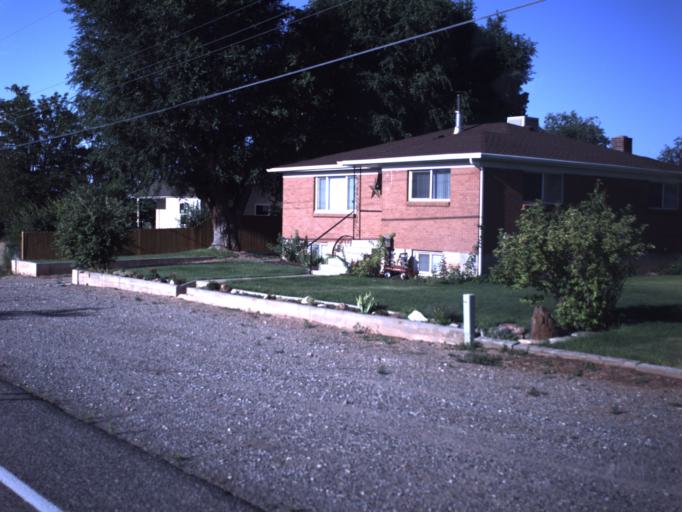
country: US
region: Utah
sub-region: Sevier County
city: Aurora
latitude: 38.8620
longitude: -111.9654
